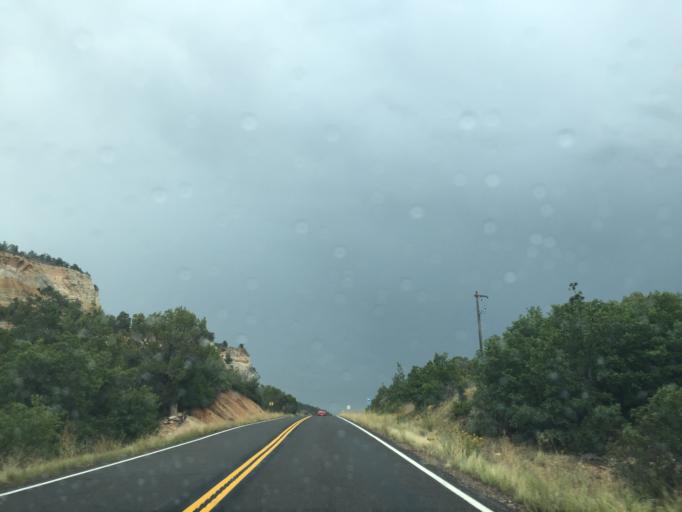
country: US
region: Utah
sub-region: Washington County
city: Hildale
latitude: 37.2356
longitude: -112.8632
